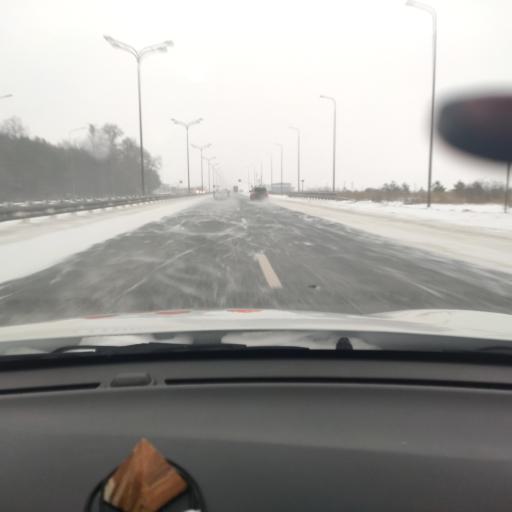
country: RU
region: Tatarstan
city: Sviyazhsk
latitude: 55.7523
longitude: 48.8034
